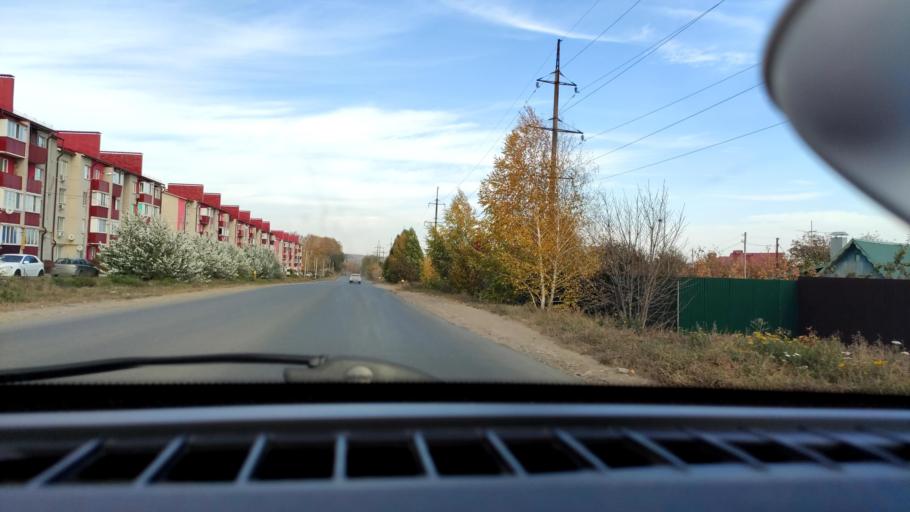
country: RU
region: Samara
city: Novosemeykino
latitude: 53.3303
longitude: 50.3142
